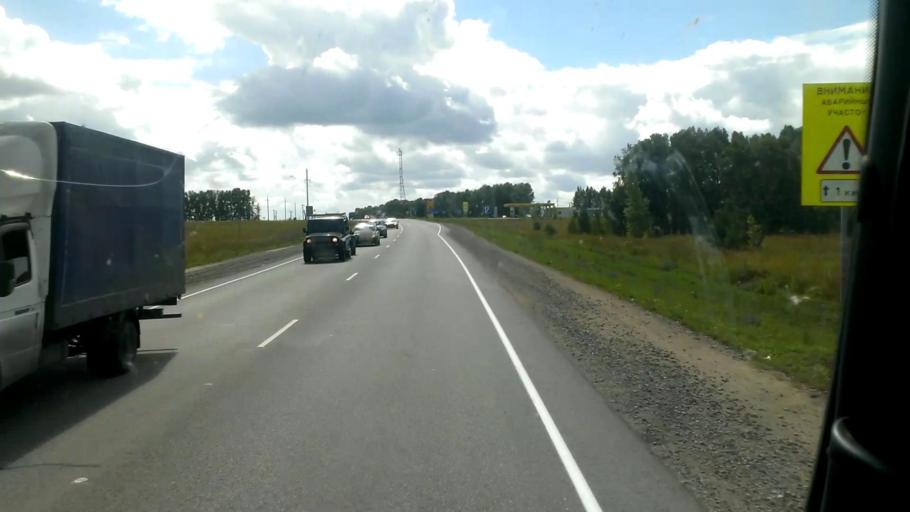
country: RU
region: Altai Krai
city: Troitskoye
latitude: 52.9709
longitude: 84.7485
